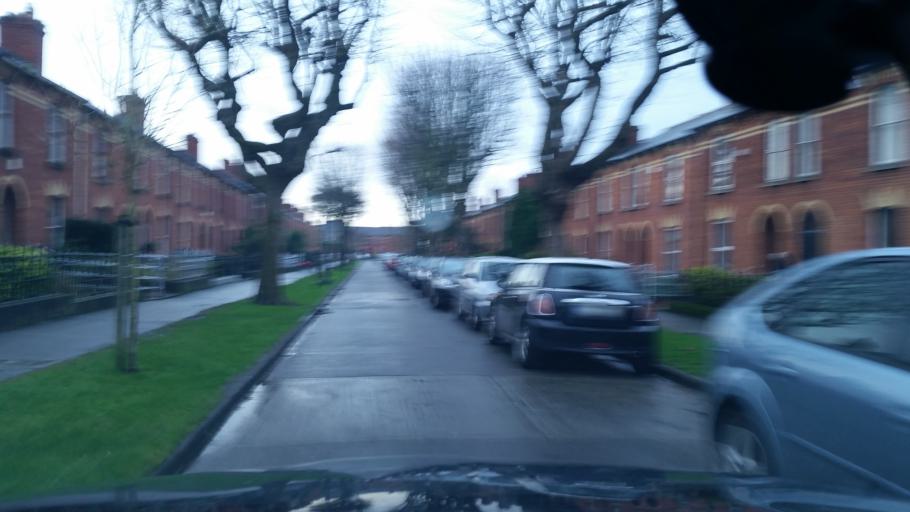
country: IE
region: Leinster
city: Cabra
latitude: 53.3653
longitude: -6.2784
